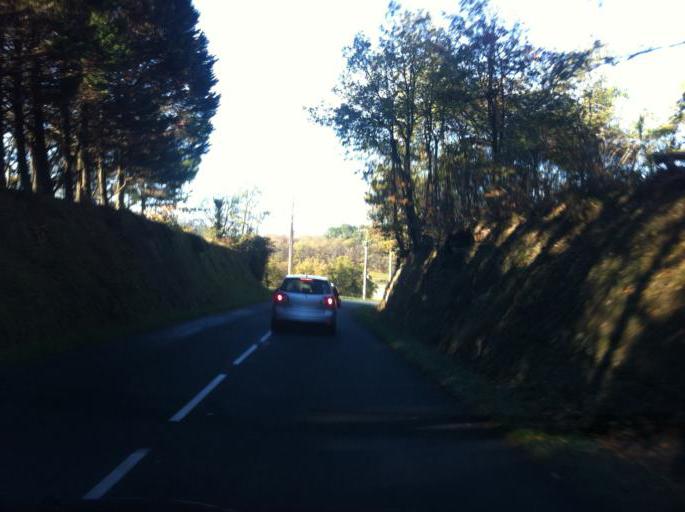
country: FR
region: Aquitaine
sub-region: Departement de la Dordogne
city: Saint-Aulaye
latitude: 45.2654
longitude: 0.1849
